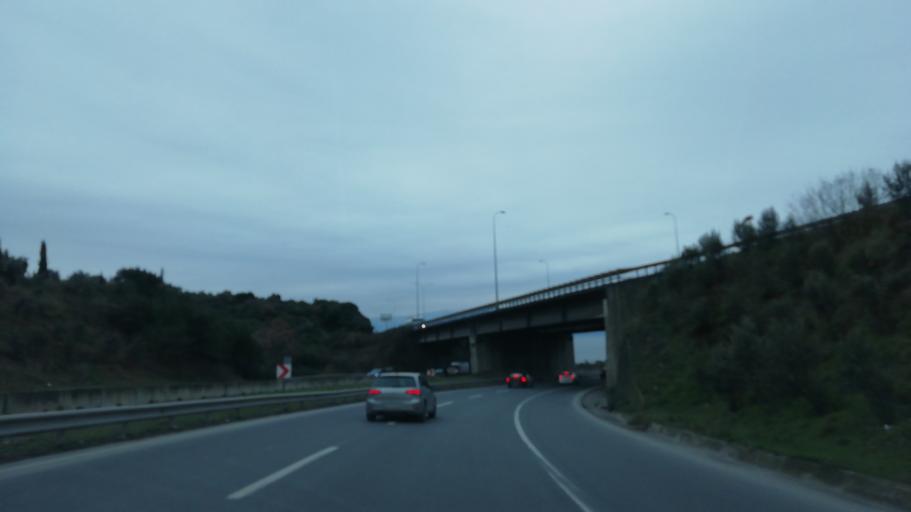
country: TR
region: Kocaeli
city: Tavsancil
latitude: 40.7727
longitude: 29.5603
